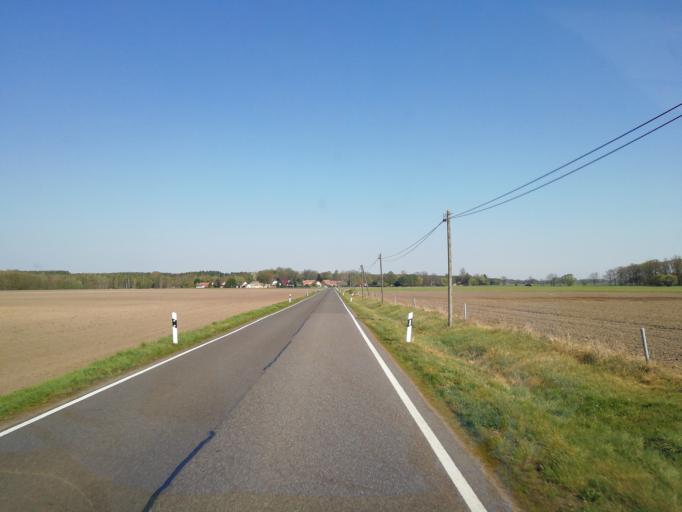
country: DE
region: Brandenburg
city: Crinitz
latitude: 51.7316
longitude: 13.8534
